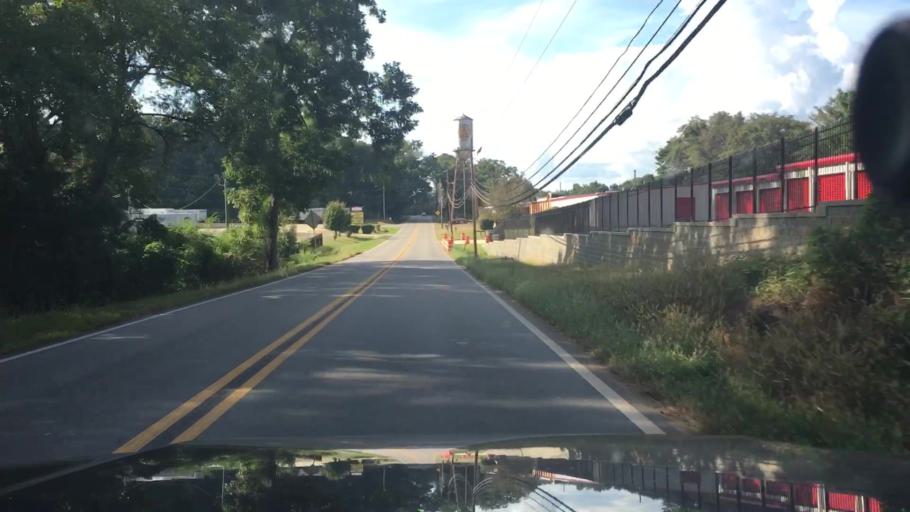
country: US
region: Georgia
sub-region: Monroe County
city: Forsyth
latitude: 33.0219
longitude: -83.9175
